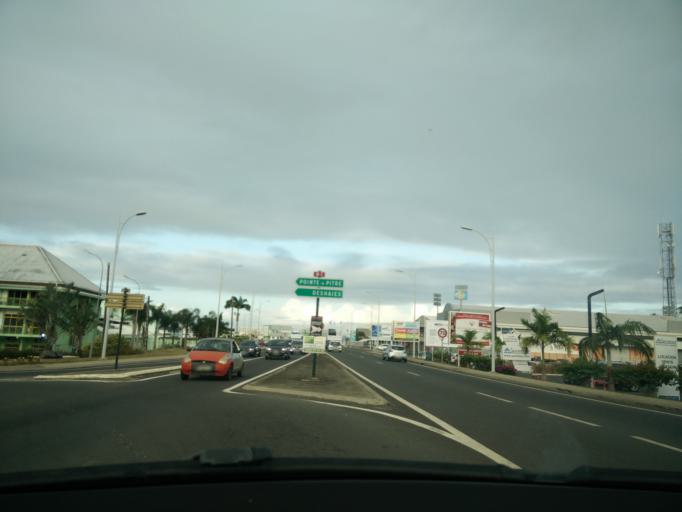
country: GP
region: Guadeloupe
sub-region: Guadeloupe
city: Baie-Mahault
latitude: 16.2404
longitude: -61.5879
